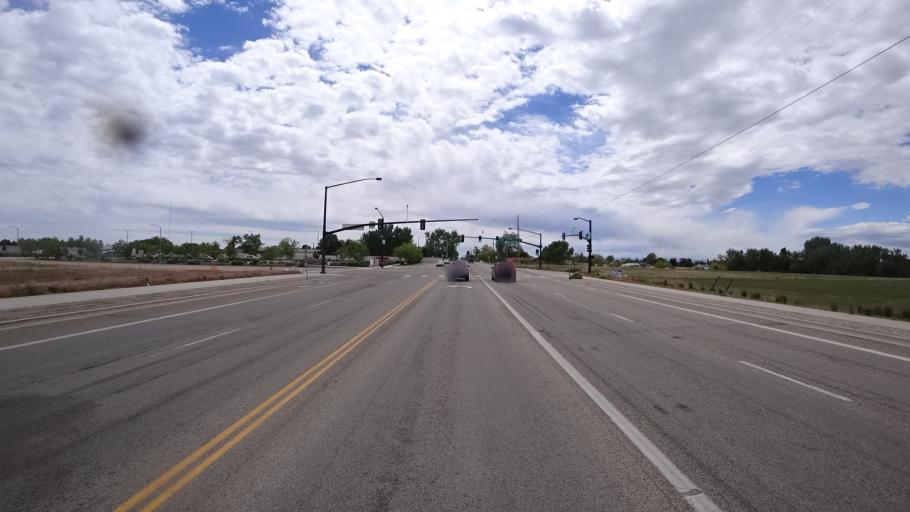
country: US
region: Idaho
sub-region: Ada County
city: Meridian
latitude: 43.5855
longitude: -116.4338
